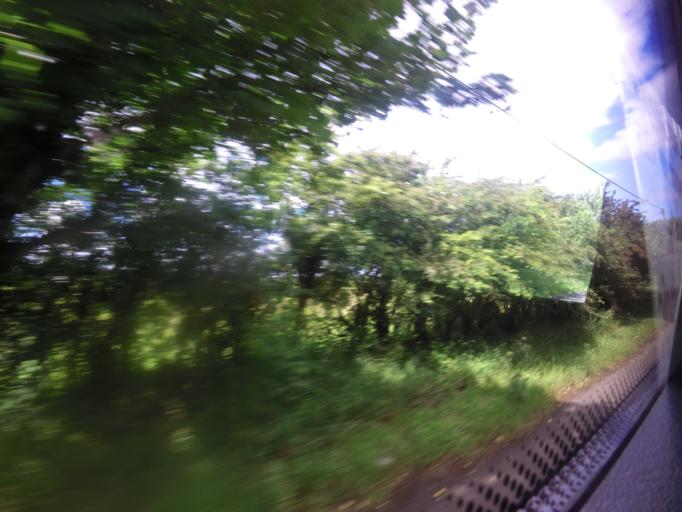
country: GB
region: England
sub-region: Norfolk
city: Cromer
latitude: 52.9064
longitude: 1.3109
